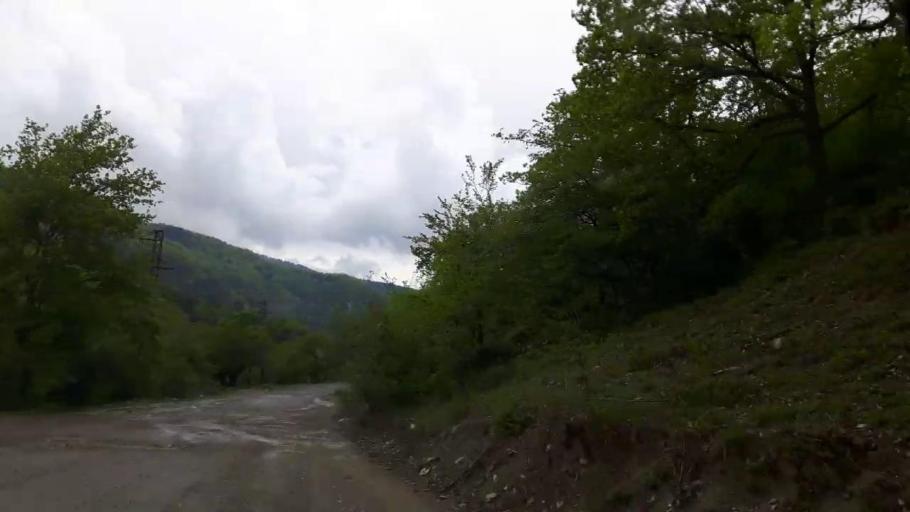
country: GE
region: Shida Kartli
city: Gori
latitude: 41.8739
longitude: 43.9878
